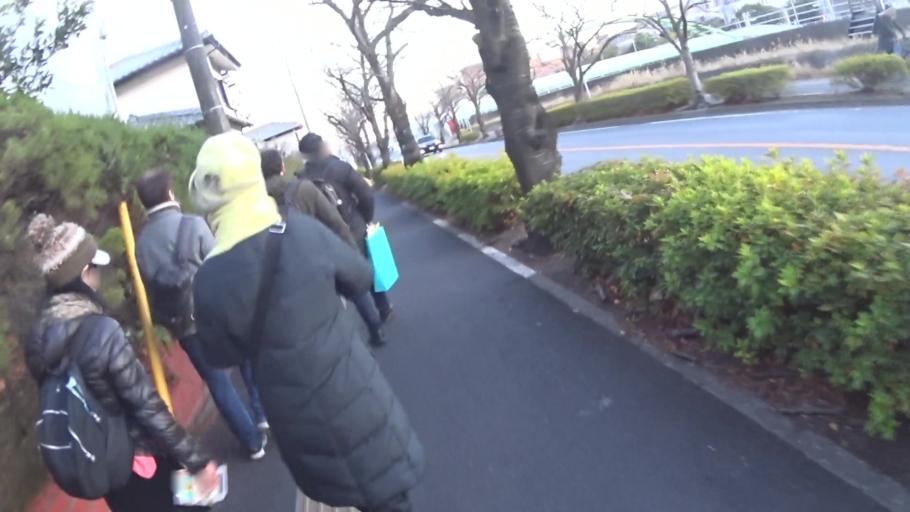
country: JP
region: Tokyo
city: Urayasu
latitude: 35.6490
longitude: 139.9054
